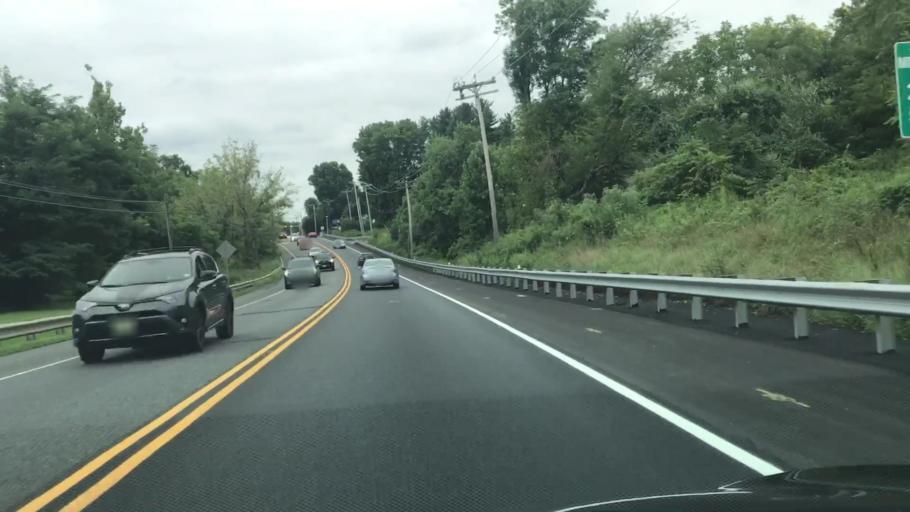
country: US
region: New Jersey
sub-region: Hunterdon County
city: Flemington
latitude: 40.5451
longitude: -74.8571
